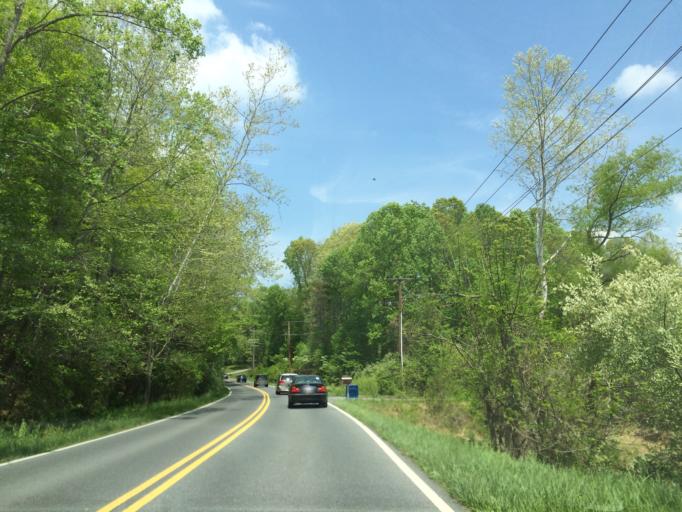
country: US
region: Maryland
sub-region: Carroll County
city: Eldersburg
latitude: 39.3723
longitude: -76.9096
